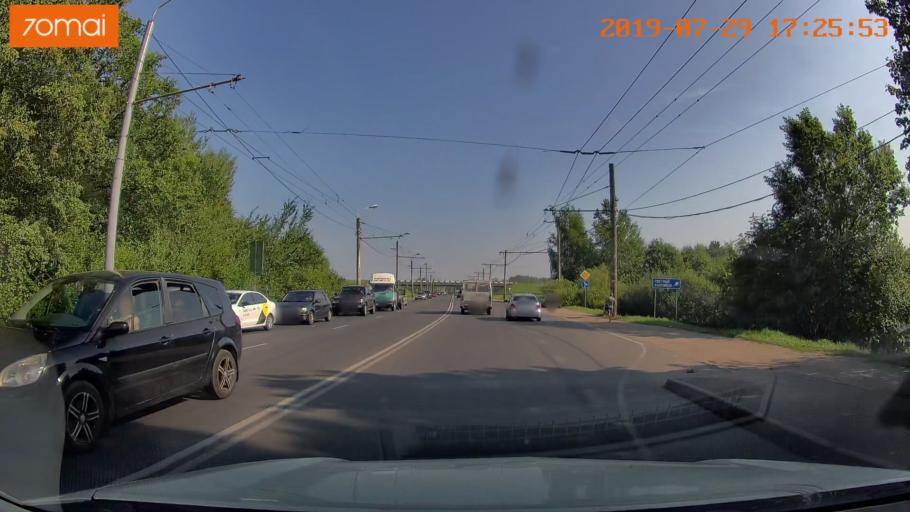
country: RU
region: Kaliningrad
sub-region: Gorod Kaliningrad
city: Kaliningrad
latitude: 54.7600
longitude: 20.4431
